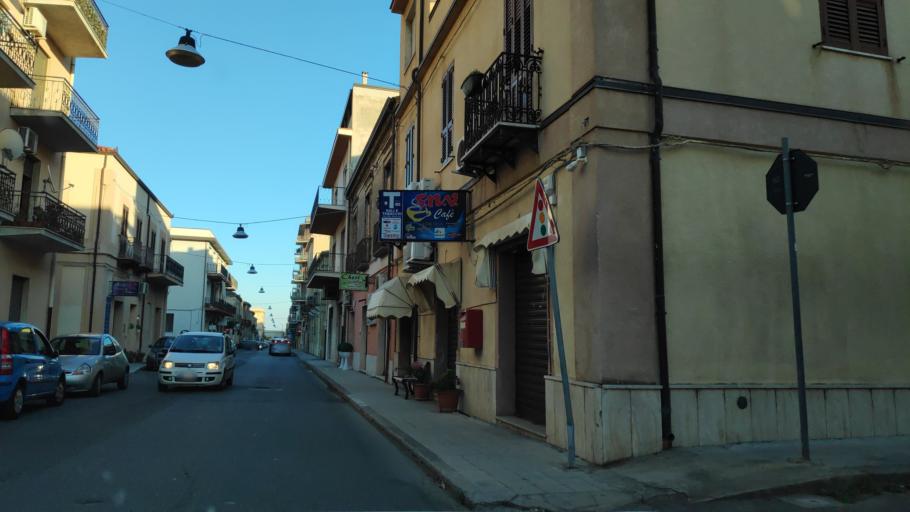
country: IT
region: Calabria
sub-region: Provincia di Reggio Calabria
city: Locri
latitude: 38.2352
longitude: 16.2614
